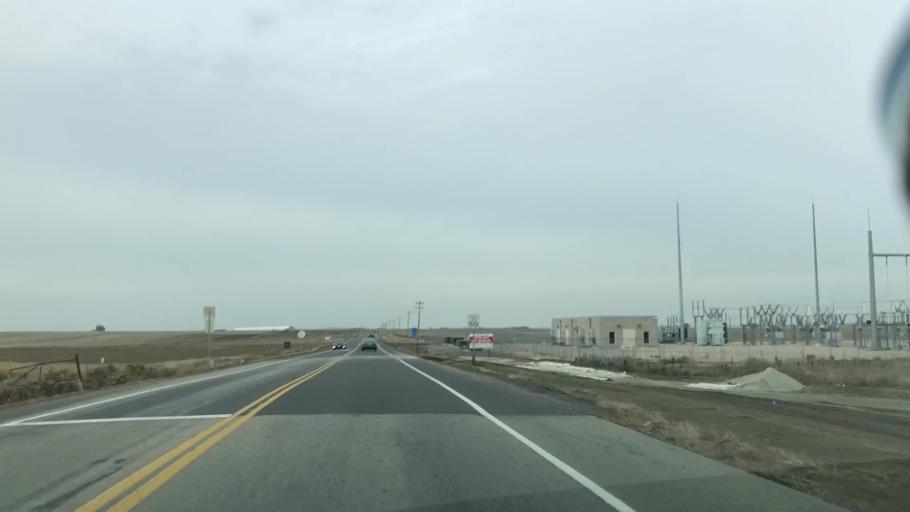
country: US
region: Colorado
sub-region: Larimer County
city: Loveland
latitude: 40.4458
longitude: -105.0204
